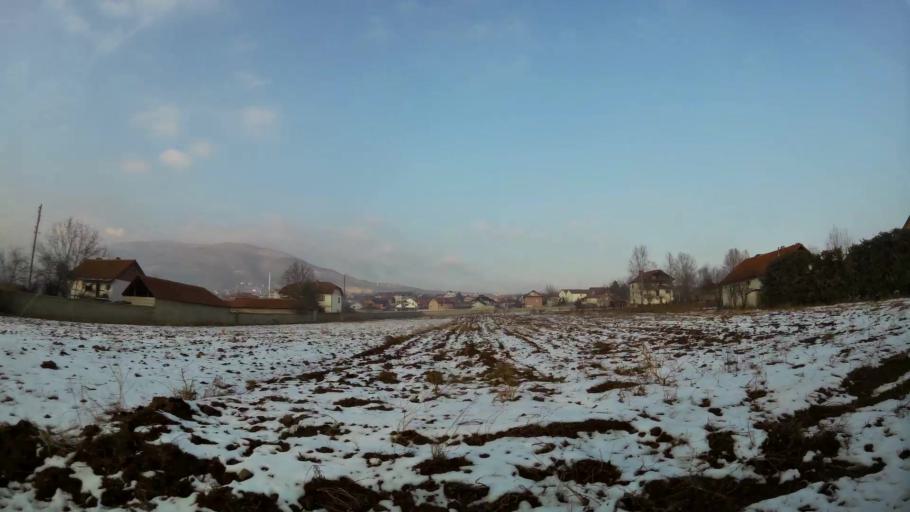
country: MK
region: Aracinovo
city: Arachinovo
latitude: 42.0198
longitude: 21.5654
